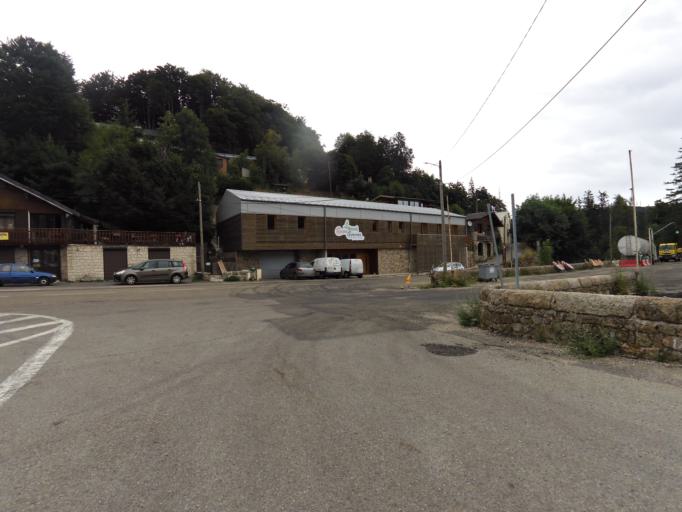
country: FR
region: Languedoc-Roussillon
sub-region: Departement du Gard
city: Valleraugue
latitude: 44.0948
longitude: 3.5494
